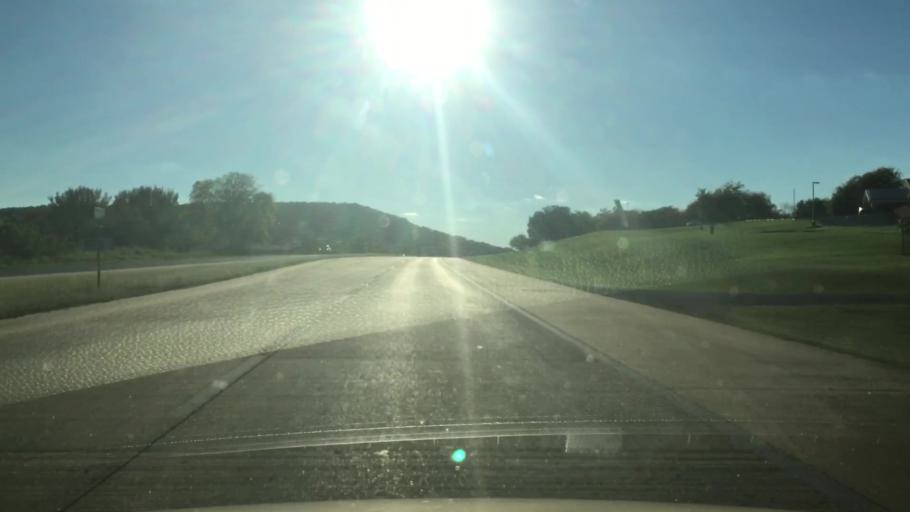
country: US
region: Oklahoma
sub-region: Cherokee County
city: Park Hill
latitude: 35.8030
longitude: -95.0873
